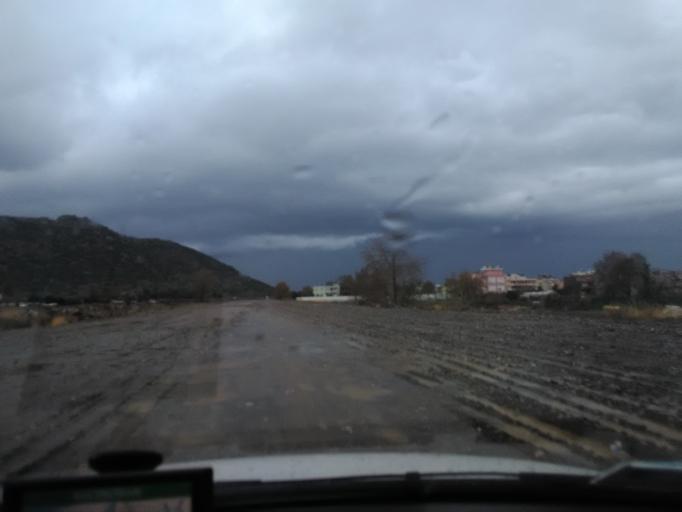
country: TR
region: Antalya
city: Gazipasa
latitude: 36.2617
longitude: 32.2951
